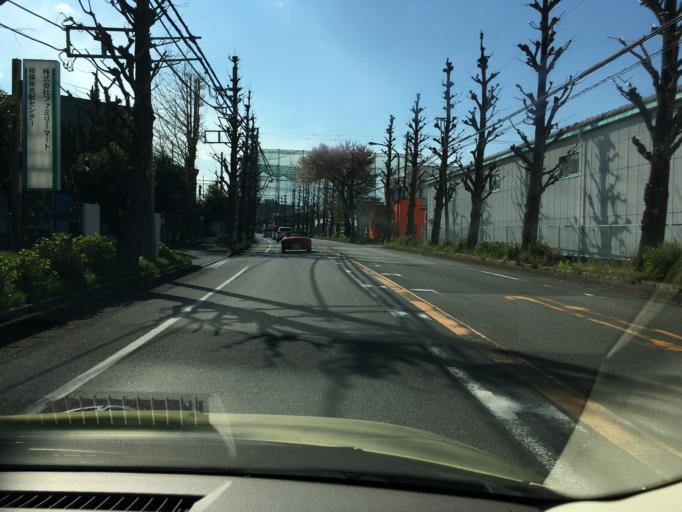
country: JP
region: Tokyo
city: Hachioji
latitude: 35.5759
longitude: 139.3575
